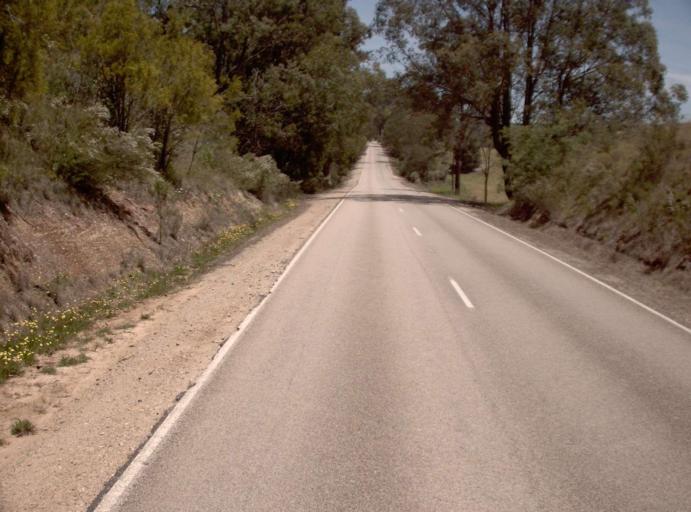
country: AU
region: Victoria
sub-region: East Gippsland
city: Lakes Entrance
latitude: -37.6725
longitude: 147.8635
